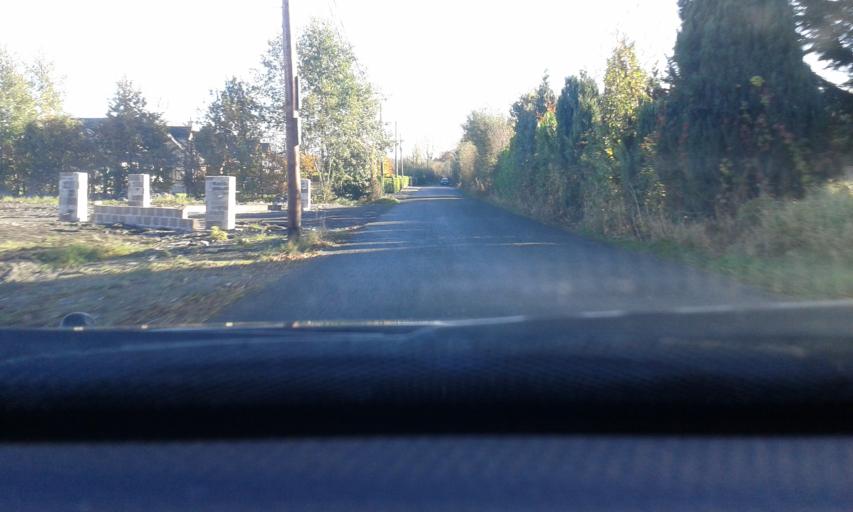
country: IE
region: Leinster
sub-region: Kildare
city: Monasterevin
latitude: 53.1435
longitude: -7.0367
